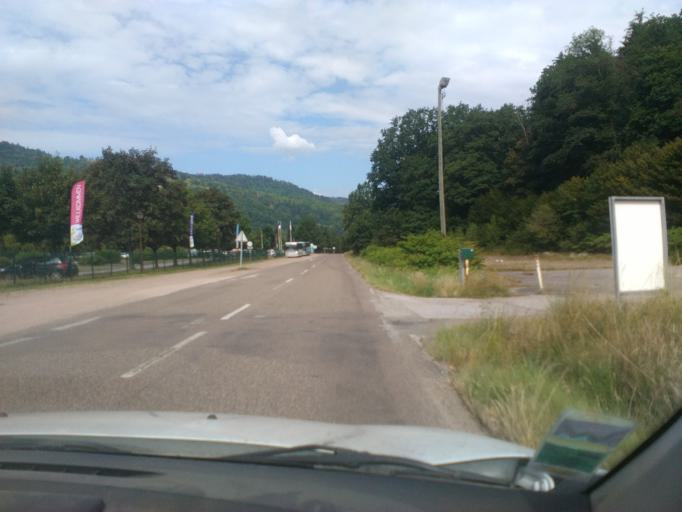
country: FR
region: Lorraine
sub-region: Departement des Vosges
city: Saulxures-sur-Moselotte
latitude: 47.9521
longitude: 6.7549
